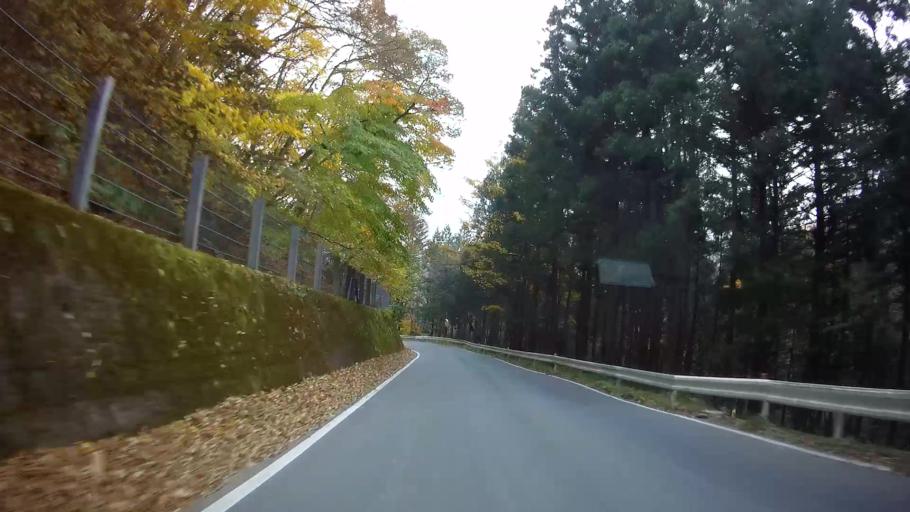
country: JP
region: Gunma
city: Nakanojomachi
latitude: 36.6569
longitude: 138.6622
